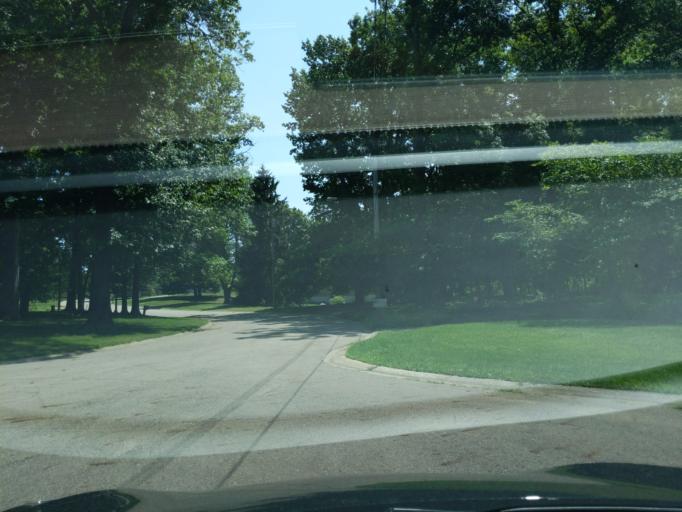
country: US
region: Michigan
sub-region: Eaton County
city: Waverly
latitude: 42.7689
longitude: -84.6164
